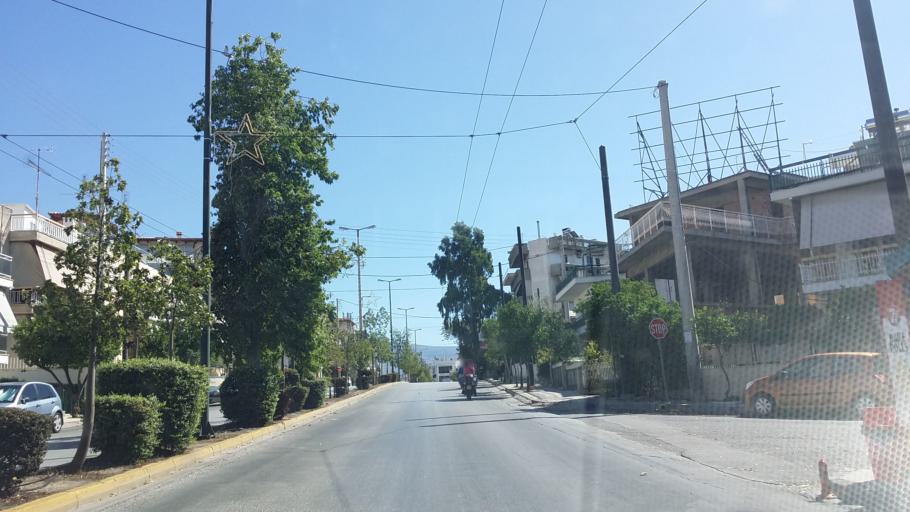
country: GR
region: Attica
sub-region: Nomarchia Athinas
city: Peristeri
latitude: 38.0170
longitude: 23.7007
